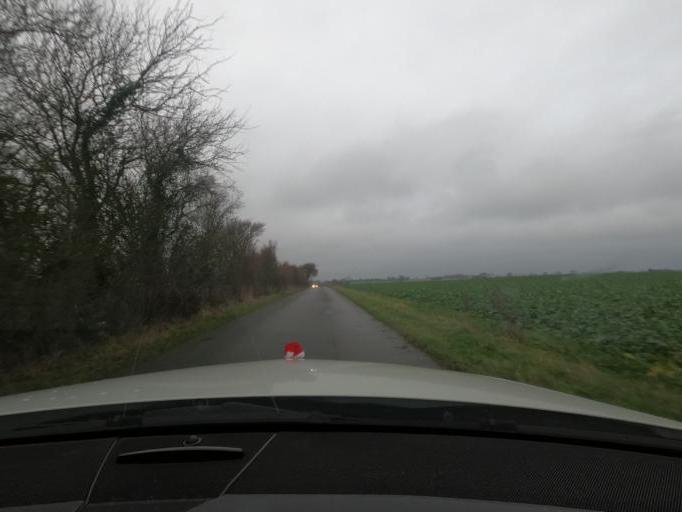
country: DK
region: South Denmark
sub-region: Haderslev Kommune
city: Starup
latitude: 55.1872
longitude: 9.6423
